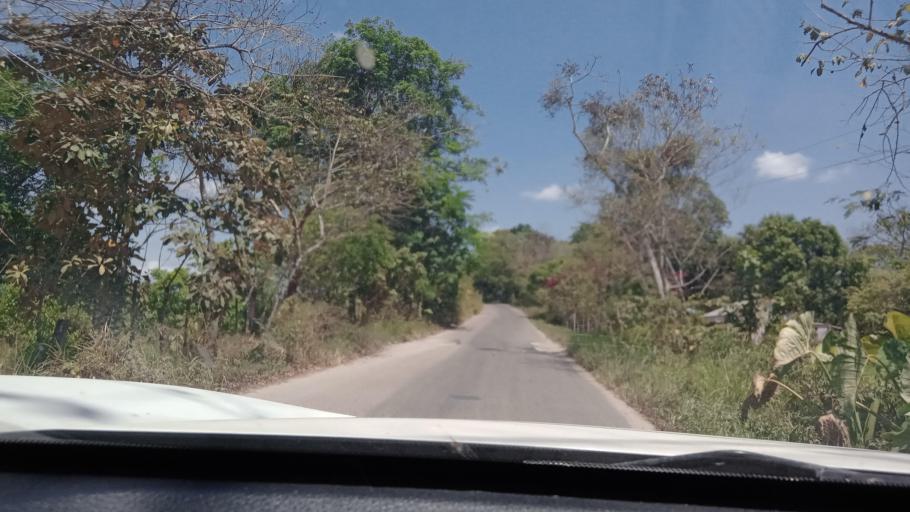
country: MX
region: Veracruz
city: Las Choapas
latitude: 17.7497
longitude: -94.1106
